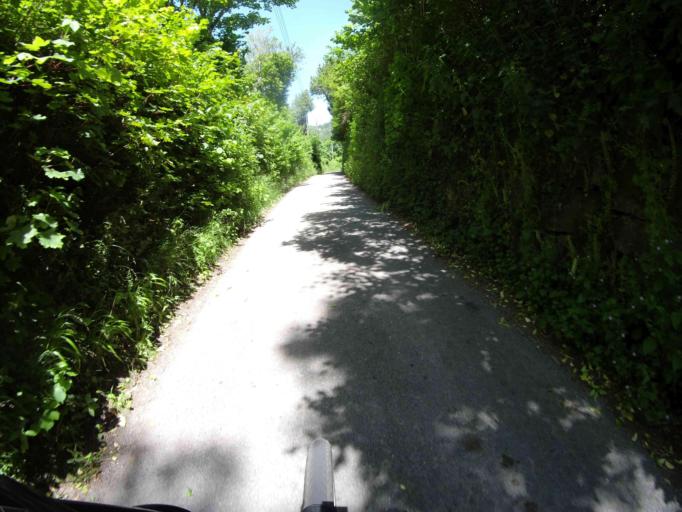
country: GB
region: England
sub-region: Devon
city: Bovey Tracey
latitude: 50.6189
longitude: -3.7140
